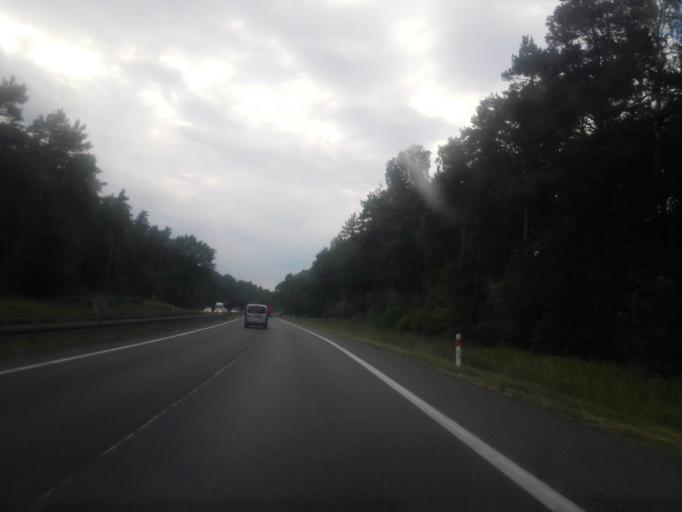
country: PL
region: Silesian Voivodeship
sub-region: Powiat myszkowski
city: Kozieglowy
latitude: 50.5374
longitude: 19.1868
